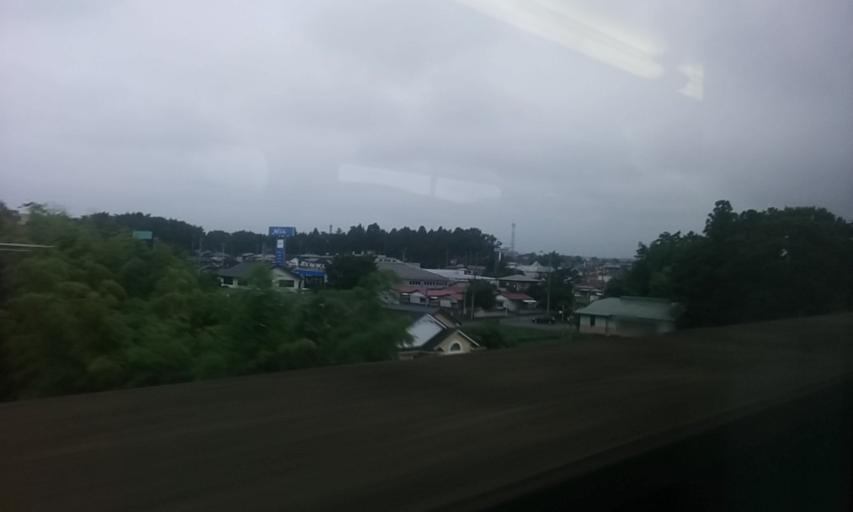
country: JP
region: Tochigi
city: Kuroiso
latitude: 36.9582
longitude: 140.0493
